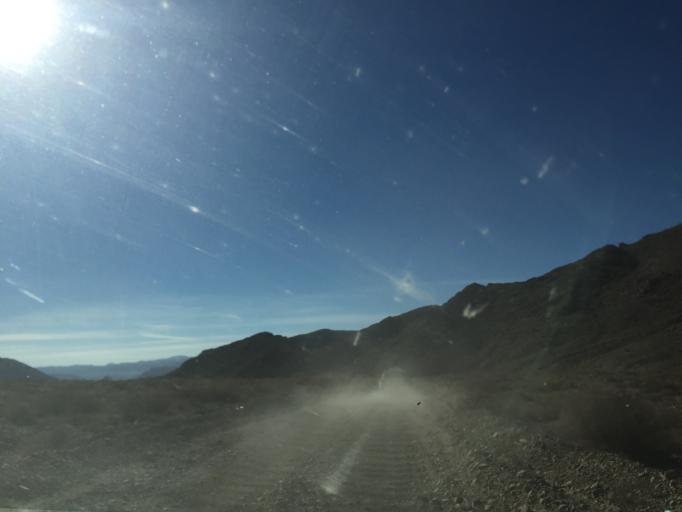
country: US
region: California
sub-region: Inyo County
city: Lone Pine
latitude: 36.8014
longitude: -117.5145
